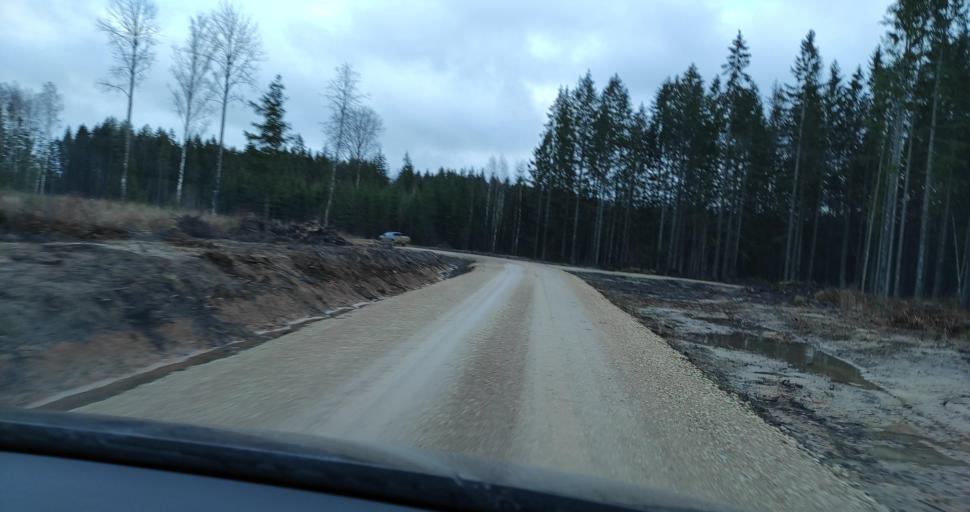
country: LV
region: Skrunda
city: Skrunda
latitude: 56.7425
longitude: 22.1996
